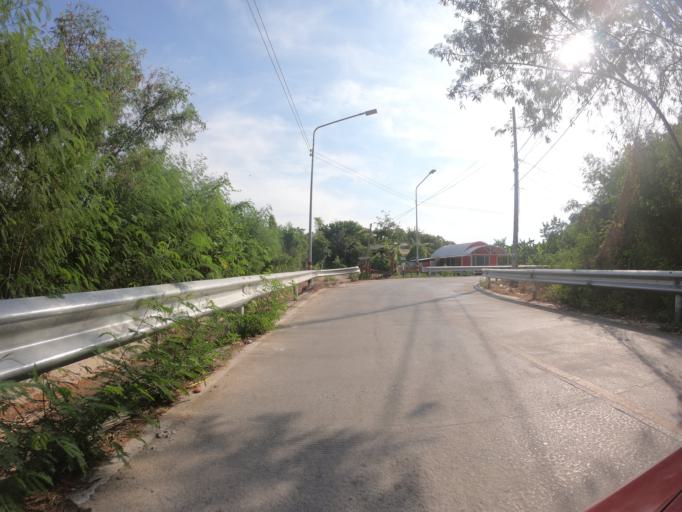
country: TH
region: Pathum Thani
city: Thanyaburi
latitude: 14.0178
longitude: 100.7334
